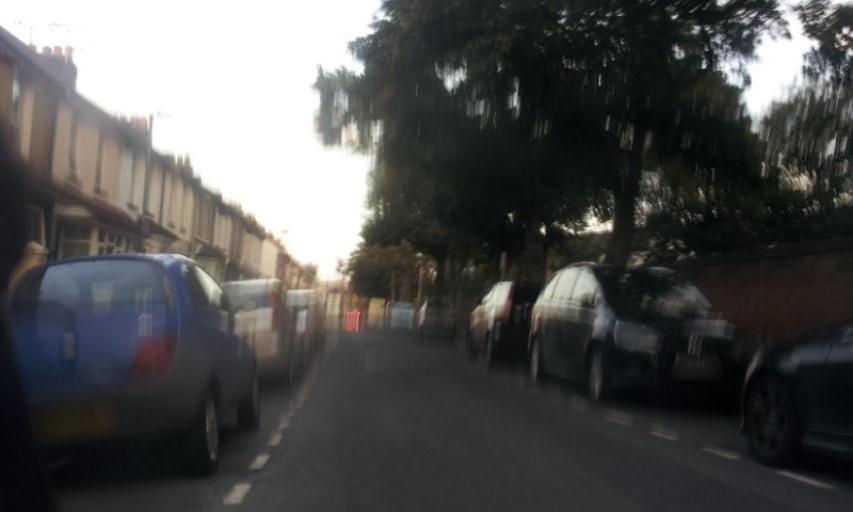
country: GB
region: England
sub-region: Kent
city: Gillingham
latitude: 51.3810
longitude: 0.5431
